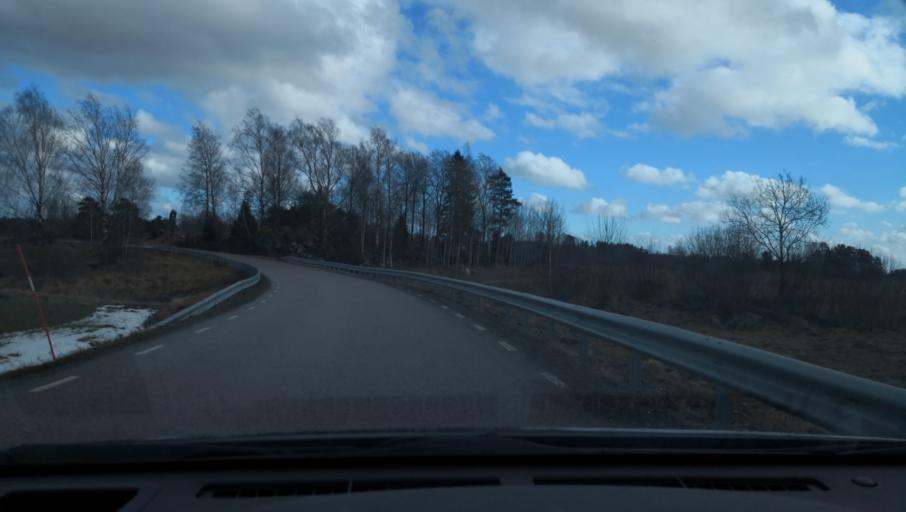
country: SE
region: OErebro
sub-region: Lindesbergs Kommun
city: Fellingsbro
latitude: 59.3502
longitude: 15.6782
